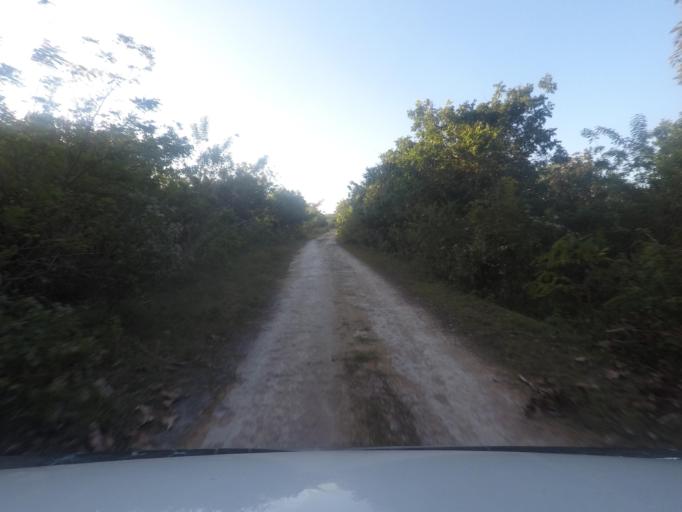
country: TL
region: Lautem
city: Lospalos
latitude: -8.4008
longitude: 127.1985
